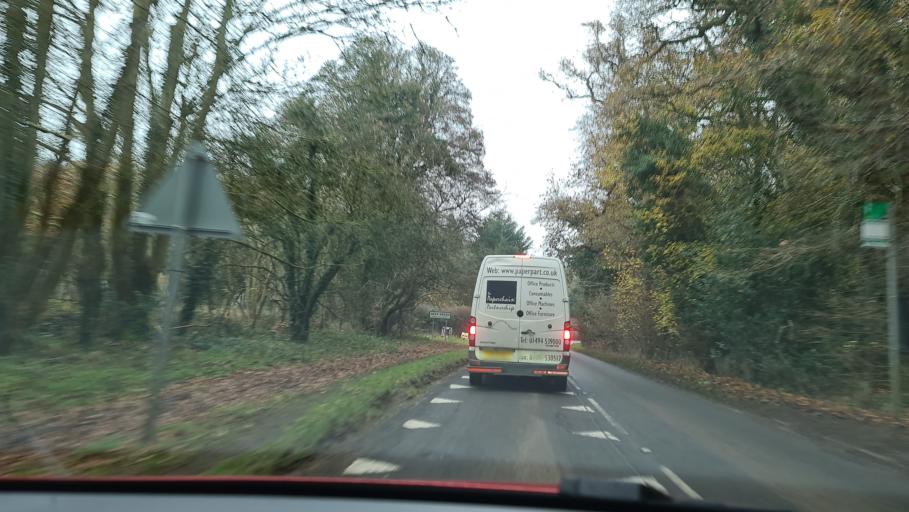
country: GB
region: England
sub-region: Buckinghamshire
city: Seer Green
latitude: 51.6139
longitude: -0.6176
